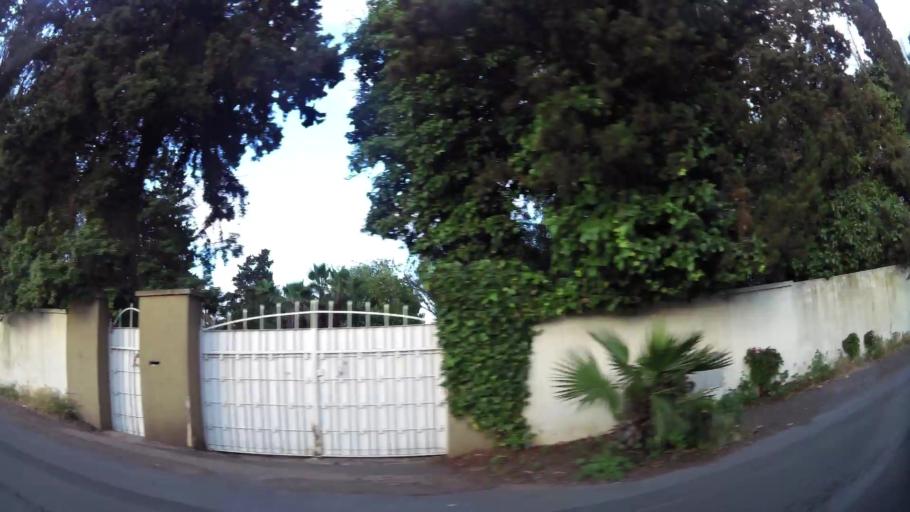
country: MA
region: Rabat-Sale-Zemmour-Zaer
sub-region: Rabat
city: Rabat
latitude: 33.9730
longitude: -6.8412
